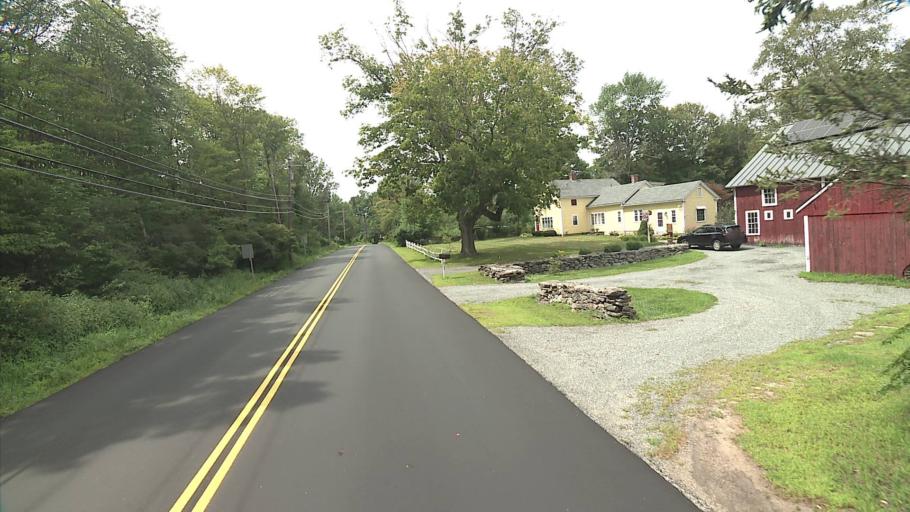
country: US
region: Connecticut
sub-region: Windham County
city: South Woodstock
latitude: 41.9544
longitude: -72.0437
